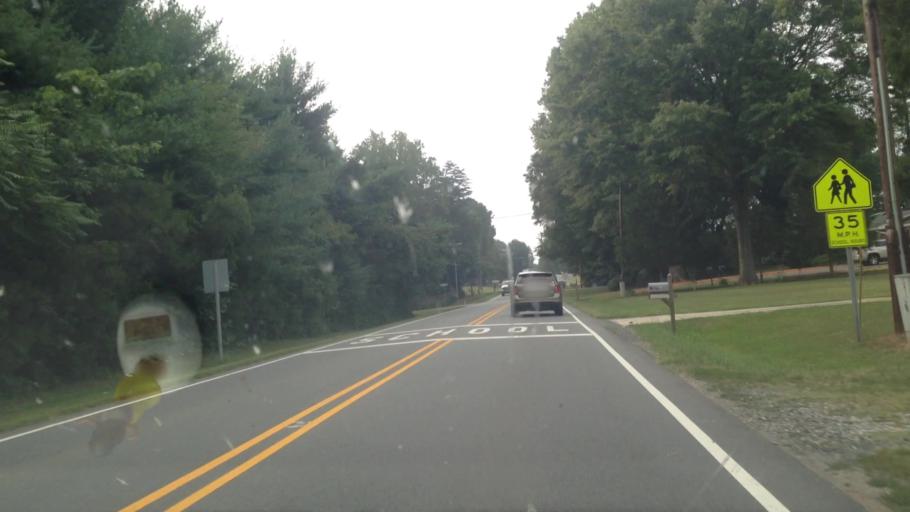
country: US
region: North Carolina
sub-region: Forsyth County
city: Walkertown
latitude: 36.1399
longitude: -80.1236
